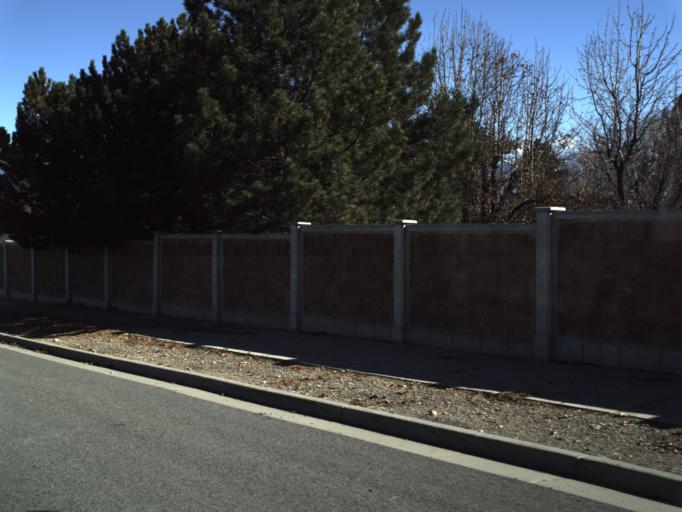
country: US
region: Utah
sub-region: Salt Lake County
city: Oquirrh
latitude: 40.5991
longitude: -112.0126
